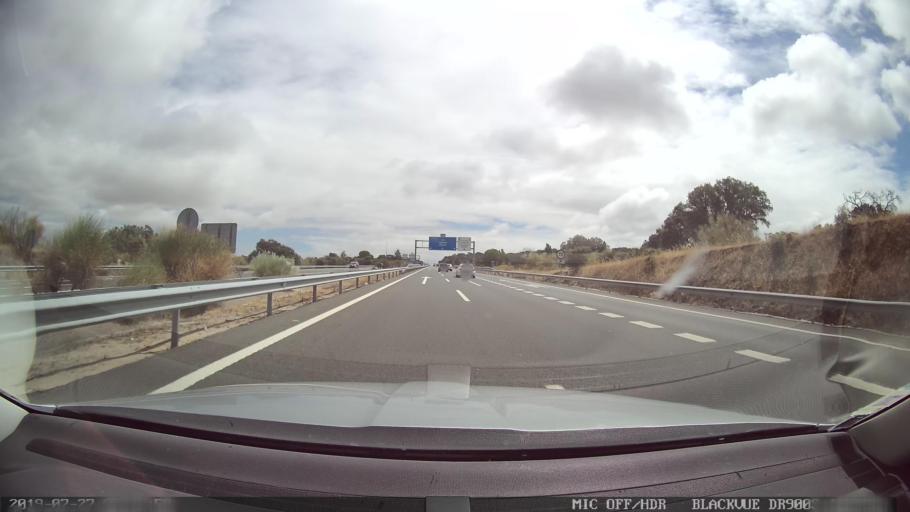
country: ES
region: Extremadura
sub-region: Provincia de Caceres
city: Millanes
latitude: 39.8718
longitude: -5.5741
